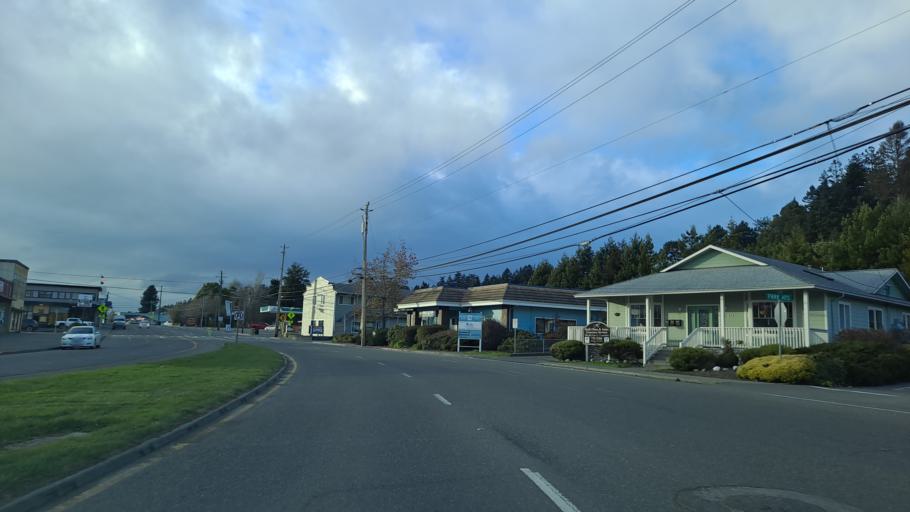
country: US
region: California
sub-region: Humboldt County
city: Fortuna
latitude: 40.5974
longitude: -124.1474
